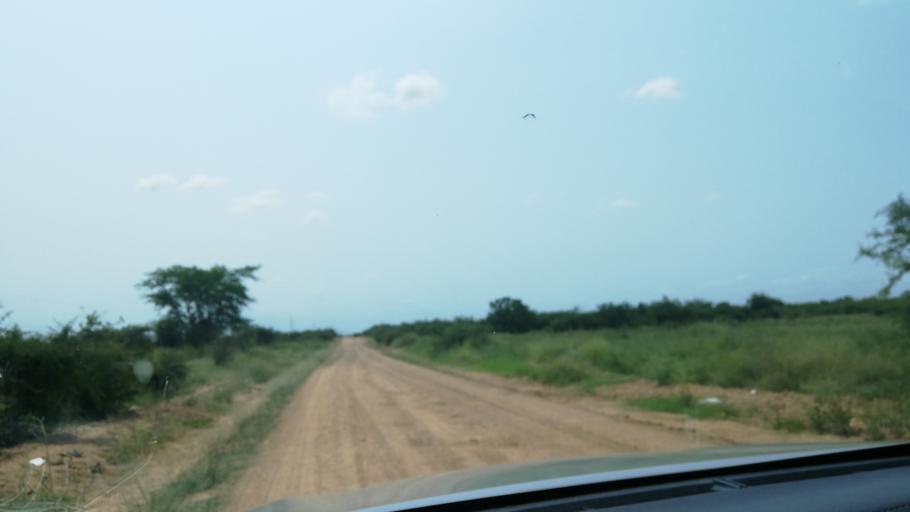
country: MZ
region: Maputo
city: Matola
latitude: -26.0805
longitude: 32.3912
